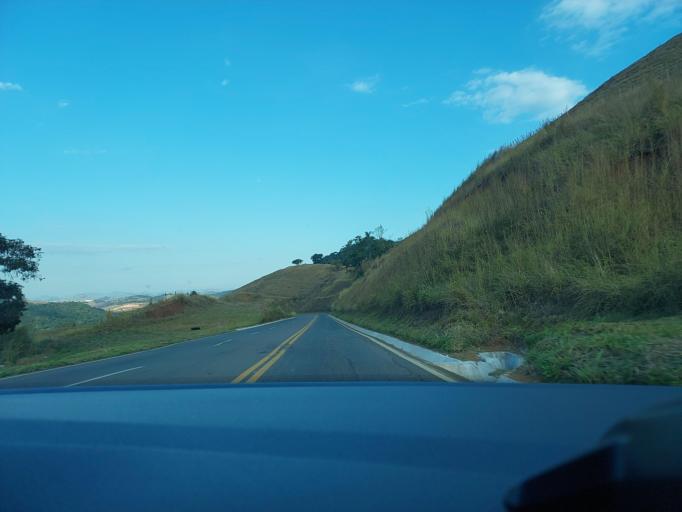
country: BR
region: Minas Gerais
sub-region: Muriae
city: Muriae
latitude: -21.0912
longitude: -42.4761
